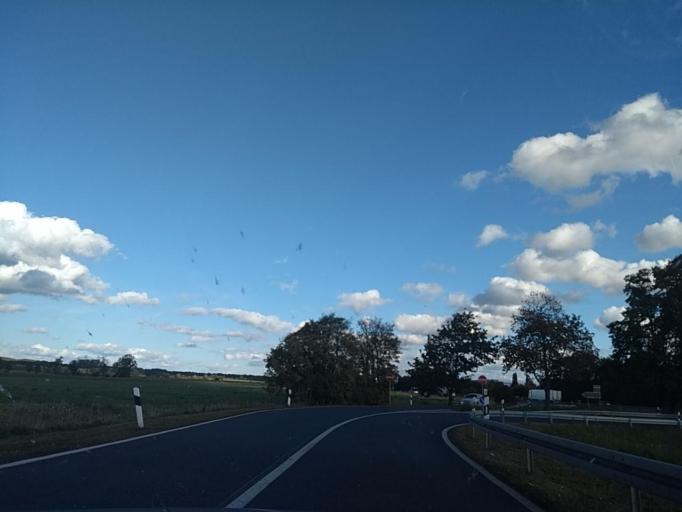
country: DE
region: Brandenburg
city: Gross Kreutz
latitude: 52.3953
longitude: 12.8389
